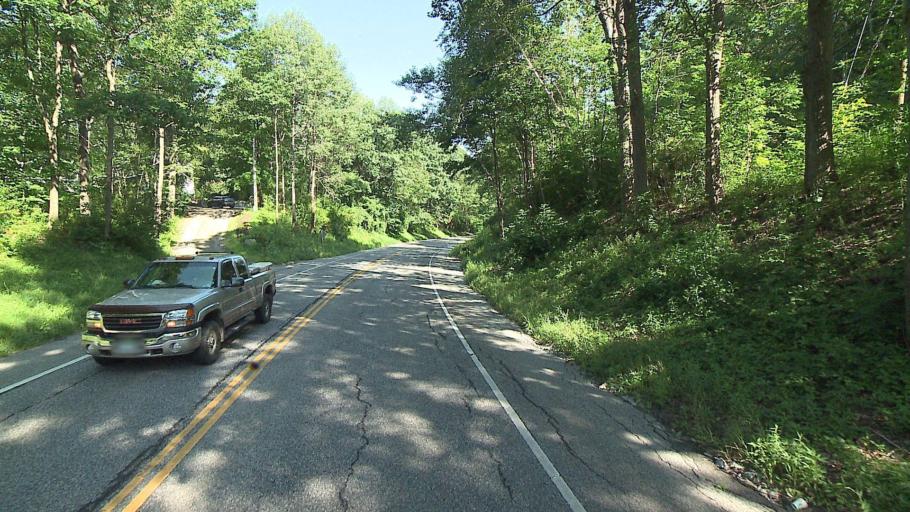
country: US
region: Connecticut
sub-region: Litchfield County
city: Kent
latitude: 41.8444
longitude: -73.4417
